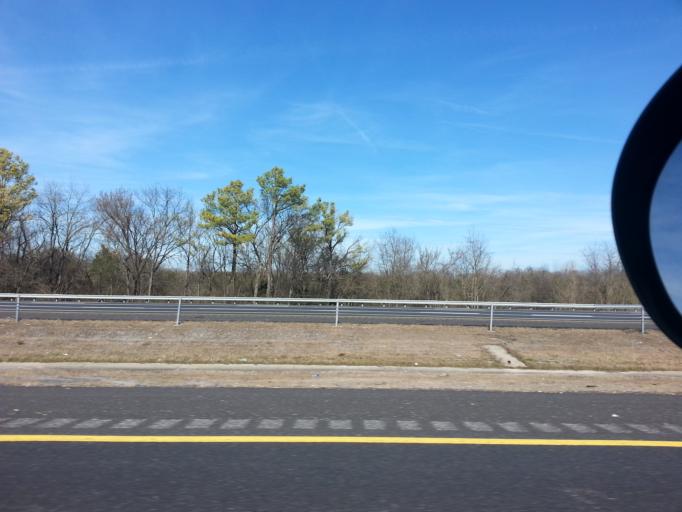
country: US
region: Tennessee
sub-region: Rutherford County
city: Murfreesboro
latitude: 35.8771
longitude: -86.4683
